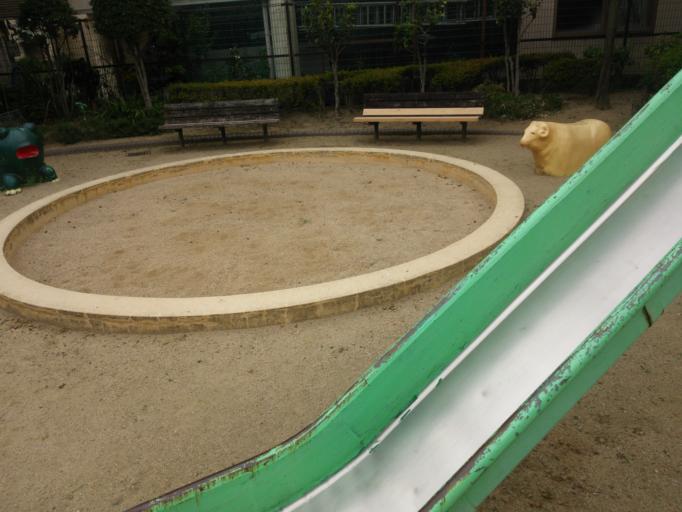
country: JP
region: Hyogo
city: Amagasaki
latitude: 34.7305
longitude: 135.4034
